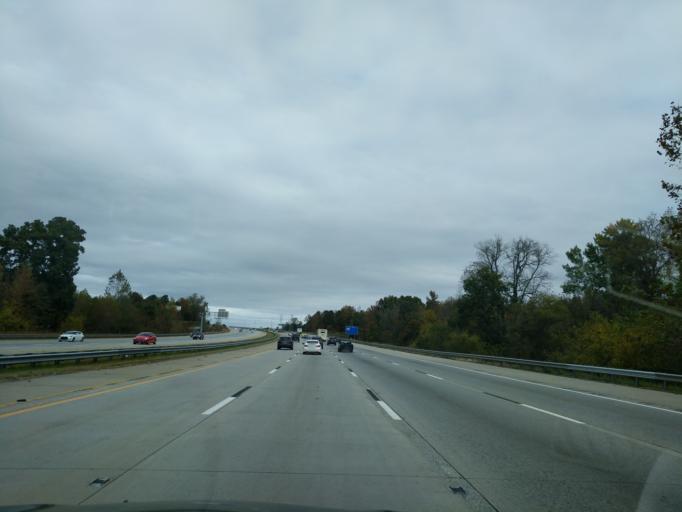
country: US
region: North Carolina
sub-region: Rowan County
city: East Spencer
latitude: 35.6857
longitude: -80.4053
